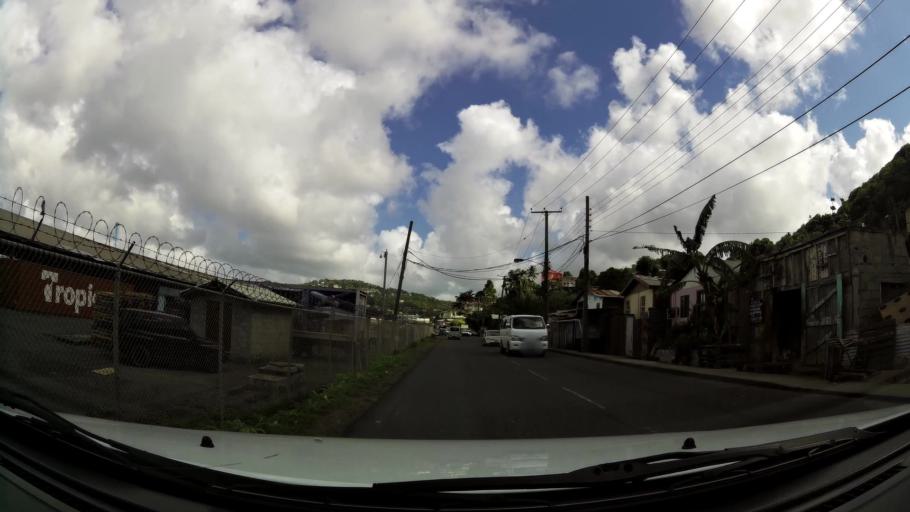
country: LC
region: Castries Quarter
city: Castries
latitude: 14.0093
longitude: -60.9964
